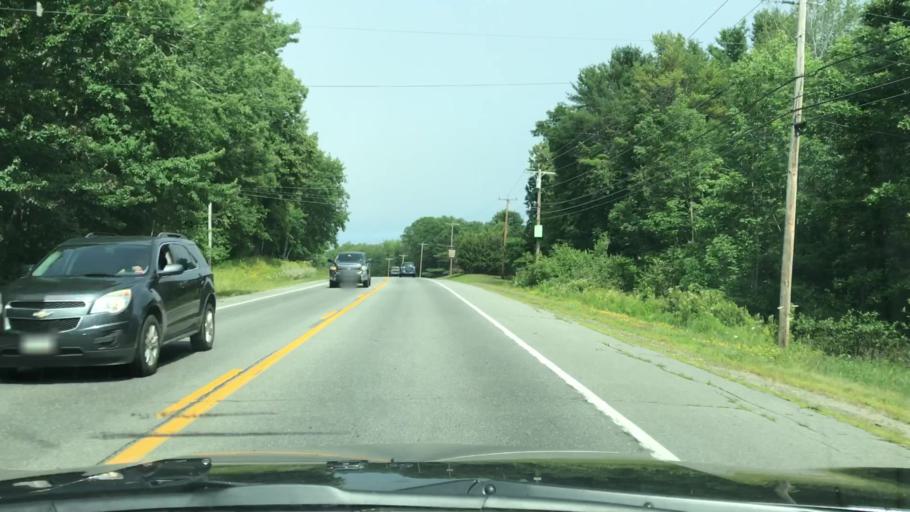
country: US
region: Maine
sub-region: Waldo County
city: Belfast
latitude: 44.4350
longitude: -68.9466
